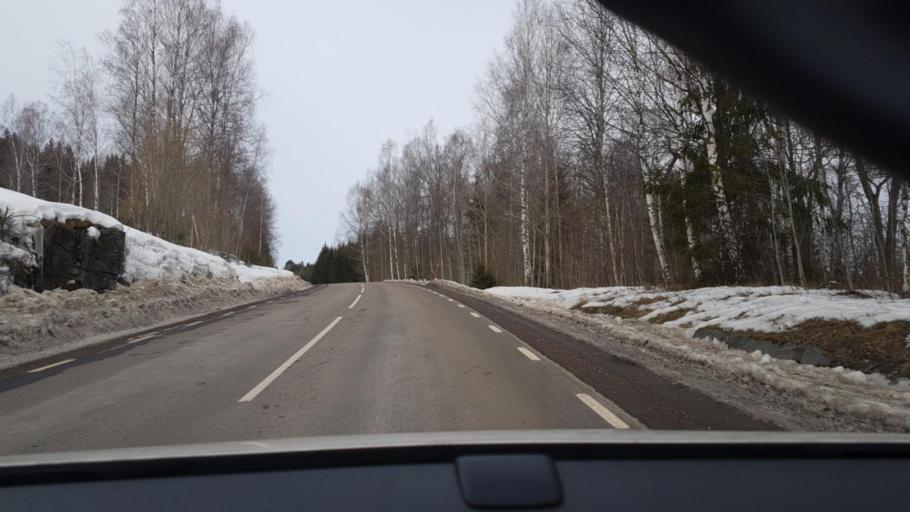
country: SE
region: Vaermland
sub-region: Eda Kommun
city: Amotfors
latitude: 59.7212
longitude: 12.4274
